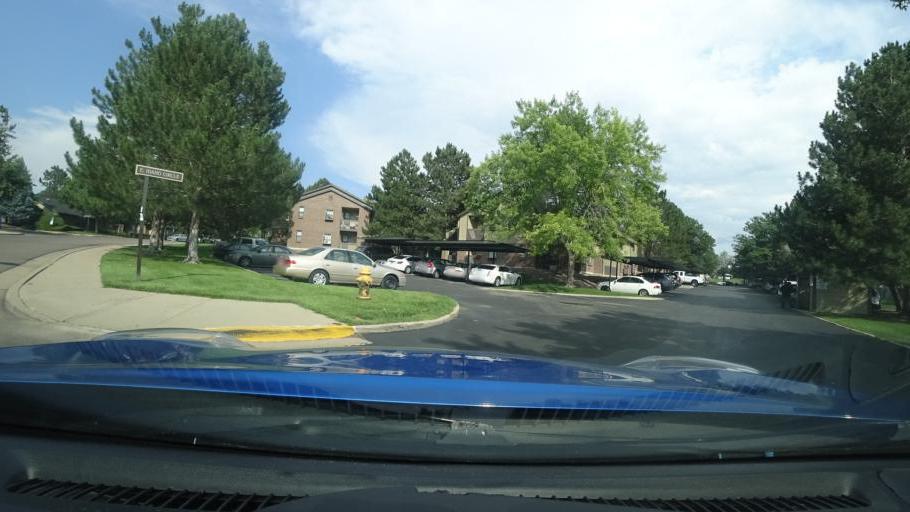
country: US
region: Colorado
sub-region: Adams County
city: Aurora
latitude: 39.6919
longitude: -104.7932
